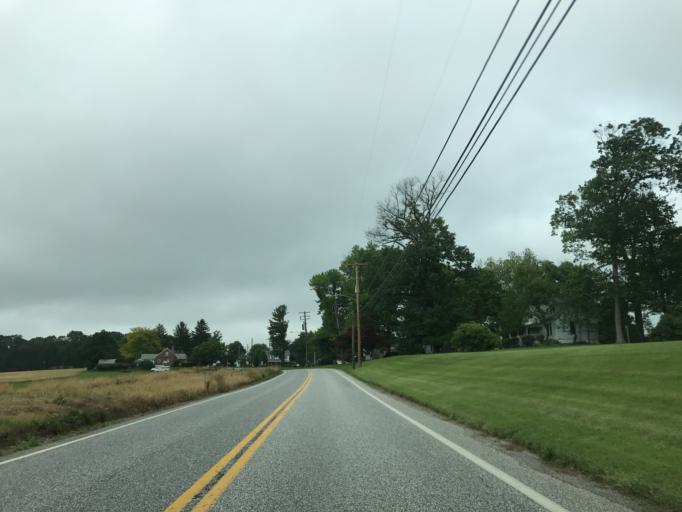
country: US
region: Pennsylvania
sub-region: York County
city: Susquehanna Trails
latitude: 39.7350
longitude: -76.4516
